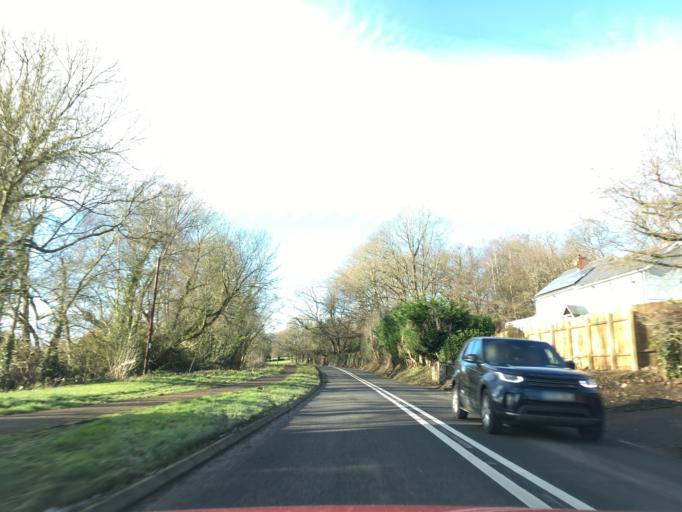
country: GB
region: Wales
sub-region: Monmouthshire
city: Usk
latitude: 51.7187
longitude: -2.9376
